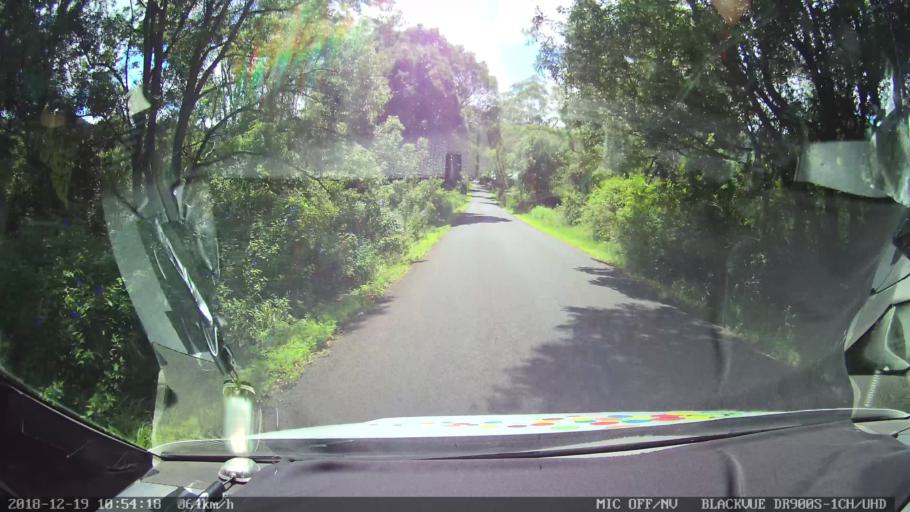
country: AU
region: New South Wales
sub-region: Lismore Municipality
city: Nimbin
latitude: -28.5940
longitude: 153.2434
